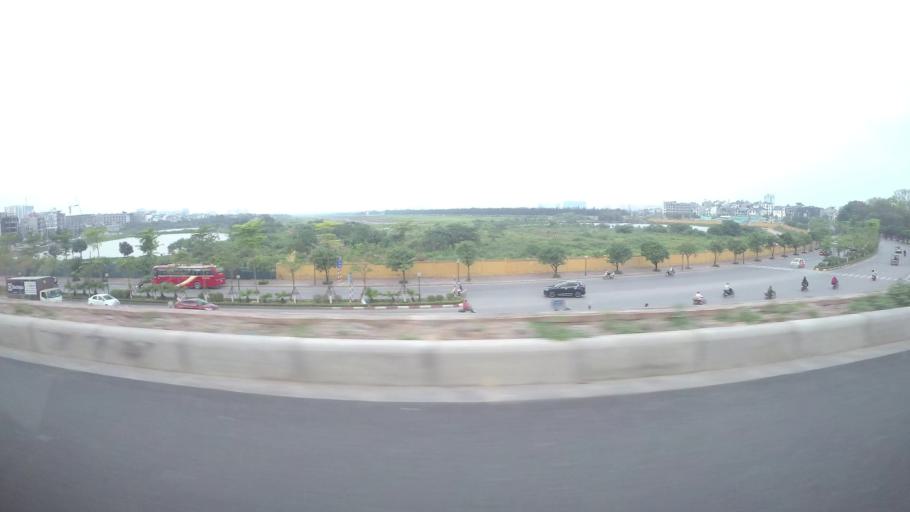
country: VN
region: Ha Noi
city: Hoan Kiem
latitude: 21.0302
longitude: 105.8801
